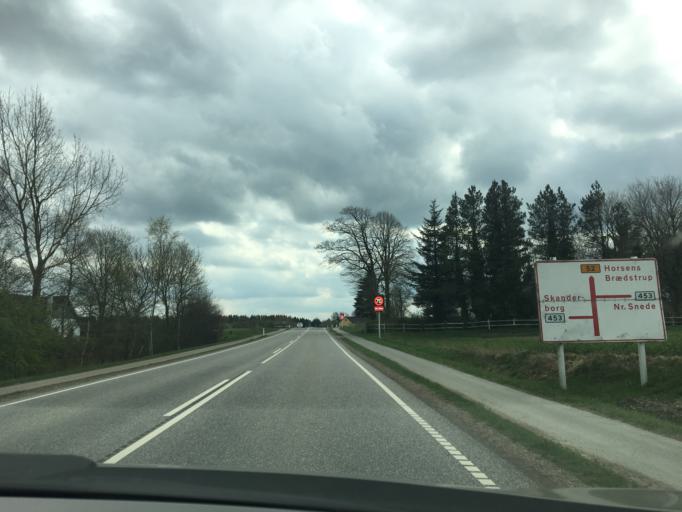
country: DK
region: Central Jutland
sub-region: Horsens Kommune
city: Braedstrup
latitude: 56.0256
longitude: 9.6100
